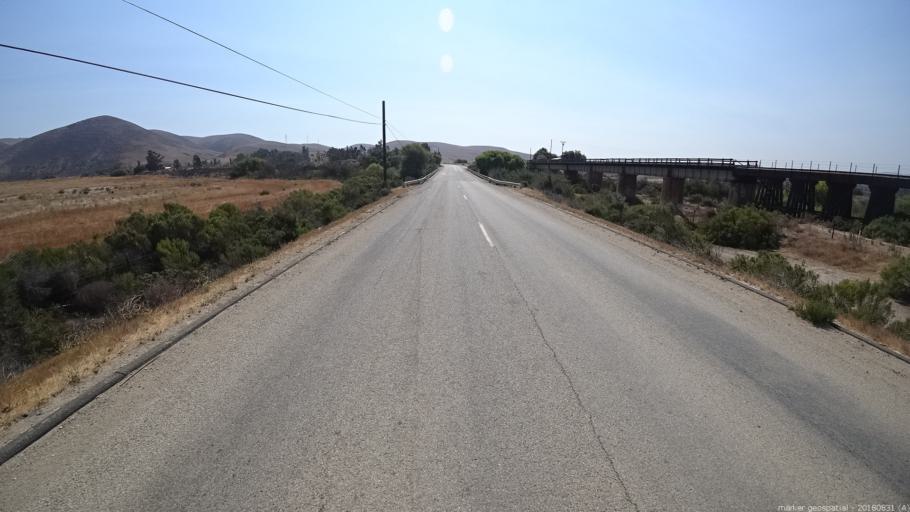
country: US
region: California
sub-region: Monterey County
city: Greenfield
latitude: 36.3541
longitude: -121.2098
